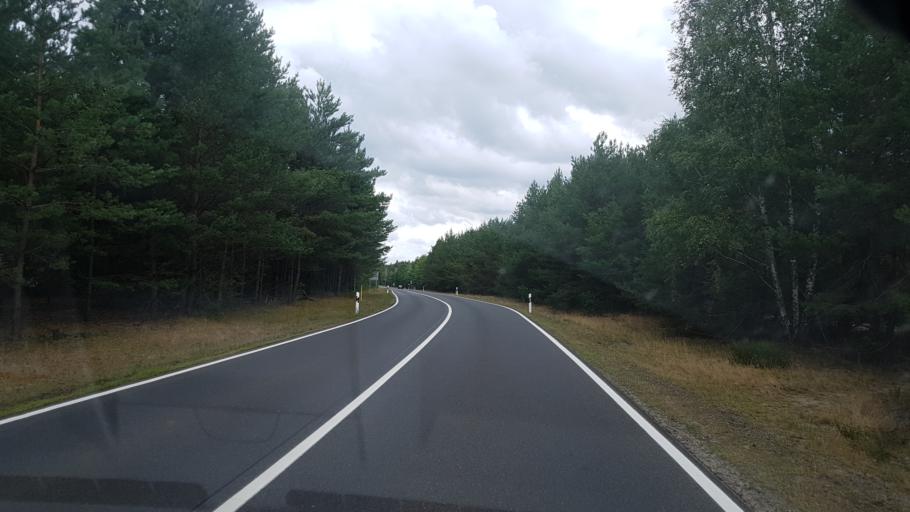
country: DE
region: Saxony
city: Boxberg
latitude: 51.3946
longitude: 14.5999
